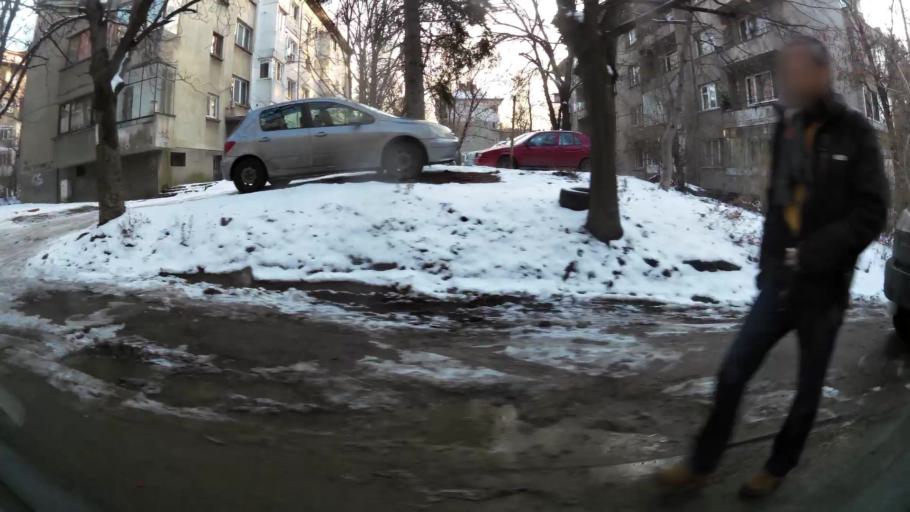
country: BG
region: Sofia-Capital
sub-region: Stolichna Obshtina
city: Sofia
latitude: 42.6921
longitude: 23.3560
